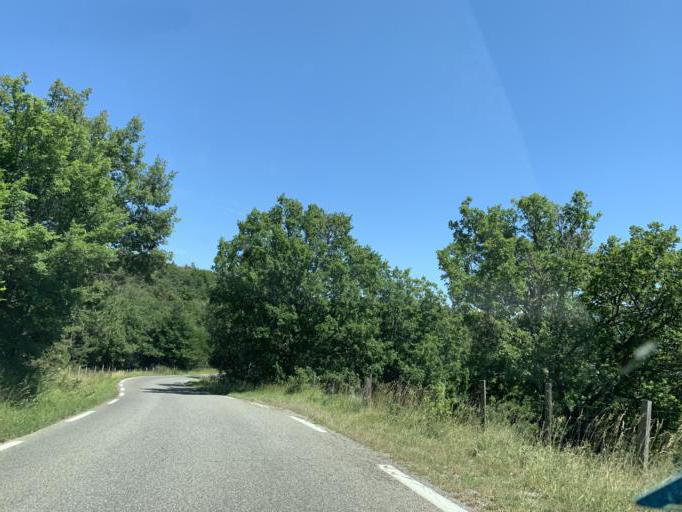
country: FR
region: Provence-Alpes-Cote d'Azur
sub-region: Departement des Hautes-Alpes
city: La Batie-Neuve
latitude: 44.5785
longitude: 6.1778
